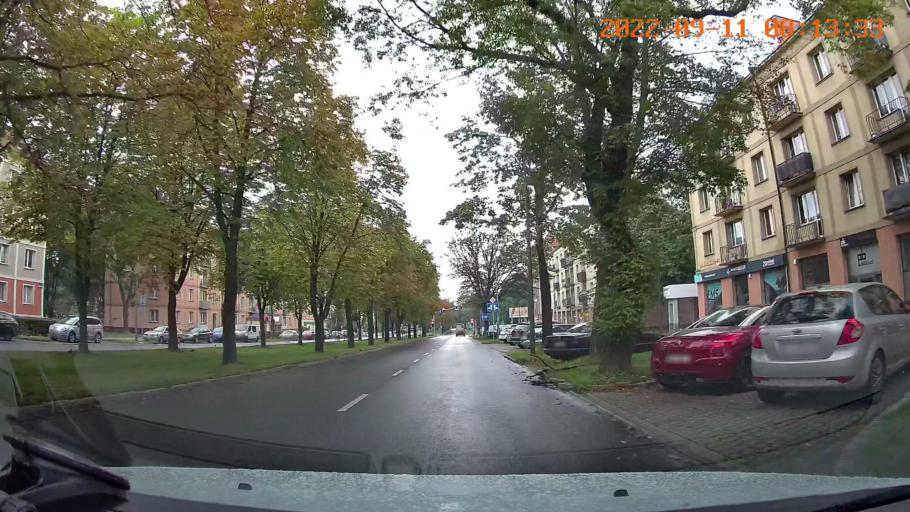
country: PL
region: Silesian Voivodeship
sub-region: Tychy
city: Tychy
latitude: 50.1207
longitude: 18.9850
